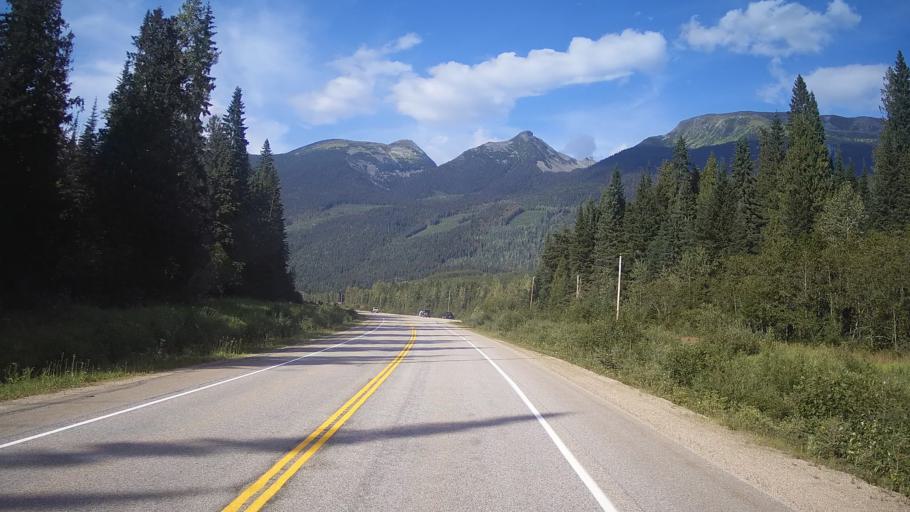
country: CA
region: Alberta
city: Jasper Park Lodge
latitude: 52.5689
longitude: -119.1024
